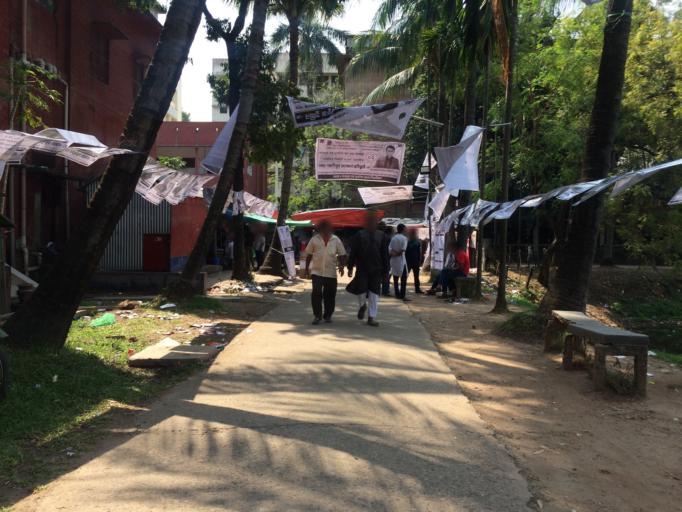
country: BD
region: Dhaka
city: Paltan
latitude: 23.7256
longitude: 90.4030
